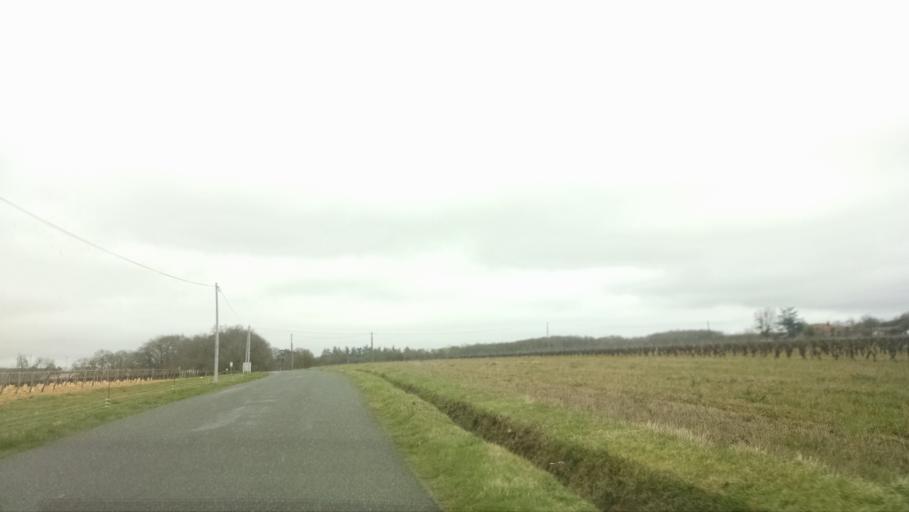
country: FR
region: Pays de la Loire
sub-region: Departement de la Loire-Atlantique
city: Vallet
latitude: 47.1942
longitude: -1.2665
